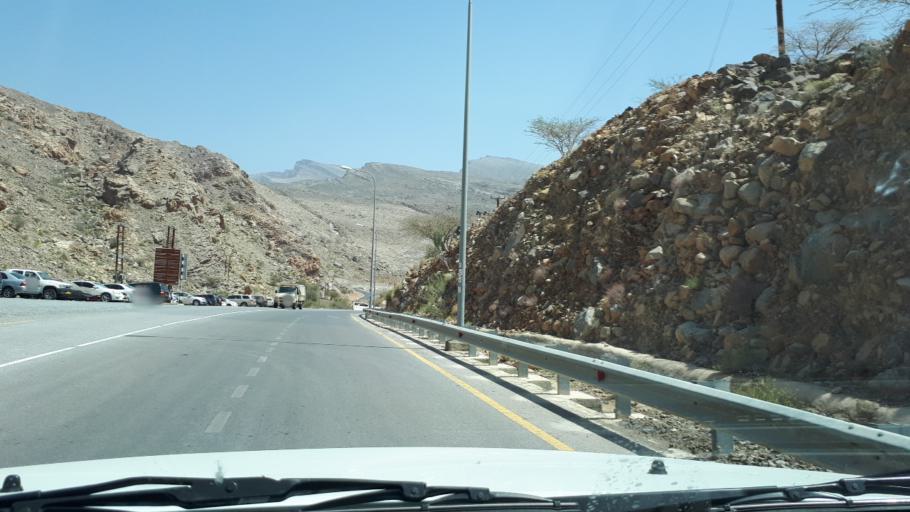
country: OM
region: Muhafazat ad Dakhiliyah
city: Izki
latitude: 22.9591
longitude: 57.6774
